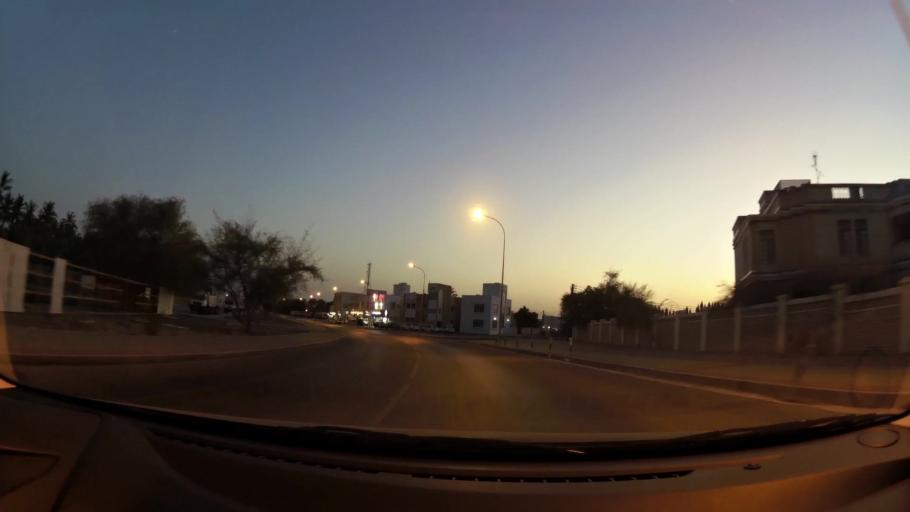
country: OM
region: Muhafazat Masqat
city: As Sib al Jadidah
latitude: 23.6688
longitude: 58.1857
